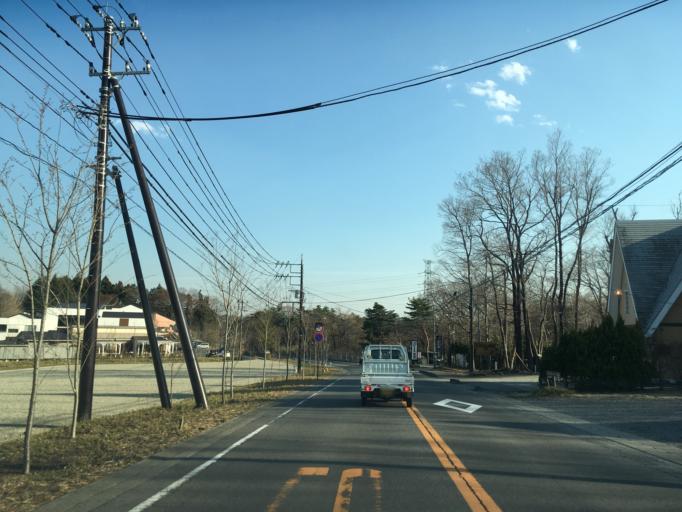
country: JP
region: Tochigi
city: Kuroiso
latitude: 37.0325
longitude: 140.0207
